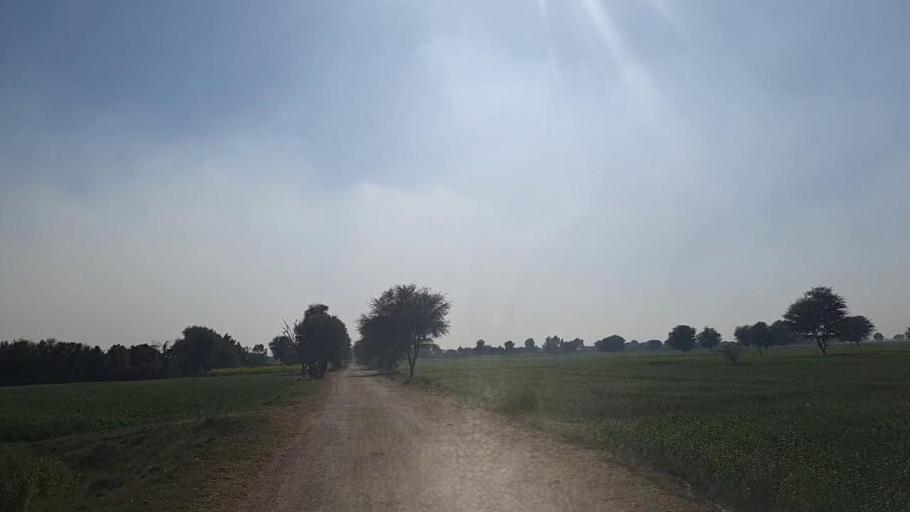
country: PK
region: Sindh
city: Shahpur Chakar
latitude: 26.1996
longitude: 68.6134
